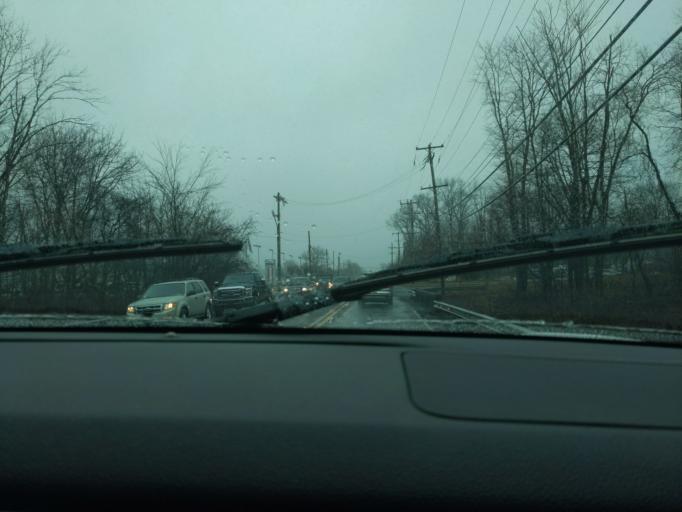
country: US
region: Pennsylvania
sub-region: Bucks County
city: Doylestown
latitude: 40.3344
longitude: -75.1398
